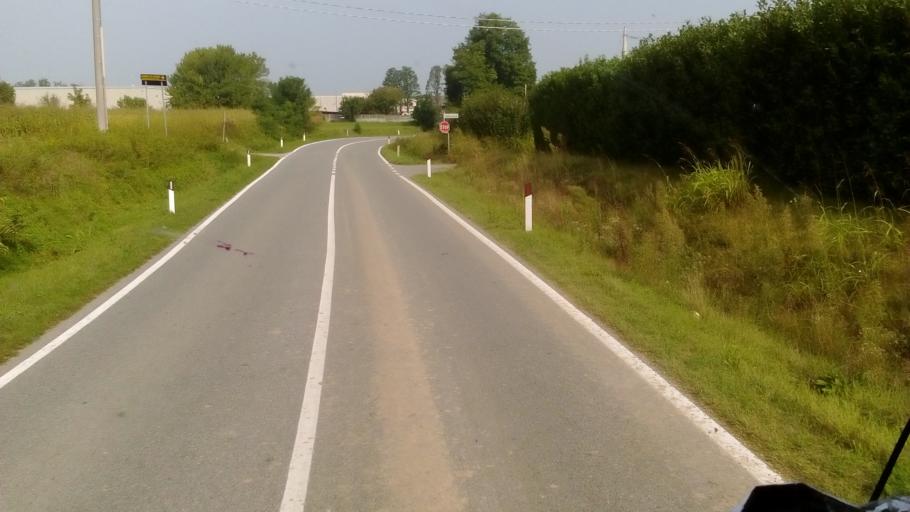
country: IT
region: Lombardy
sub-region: Provincia di Como
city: San Michele-San Giorgio
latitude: 45.6830
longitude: 9.0547
